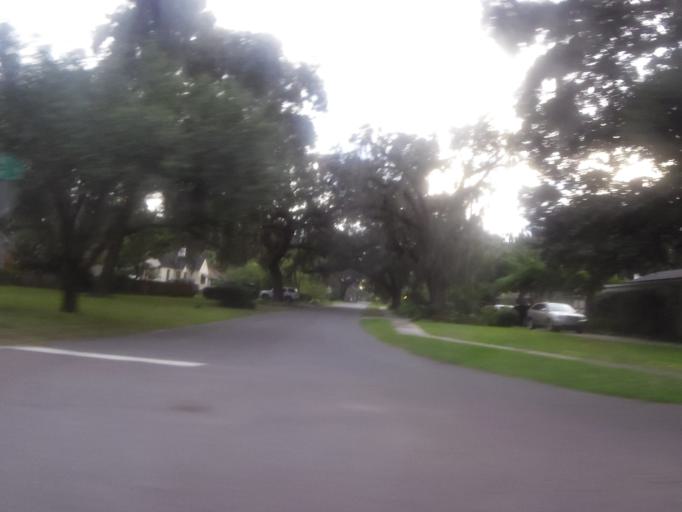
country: US
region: Florida
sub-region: Duval County
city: Jacksonville
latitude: 30.2777
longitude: -81.7009
